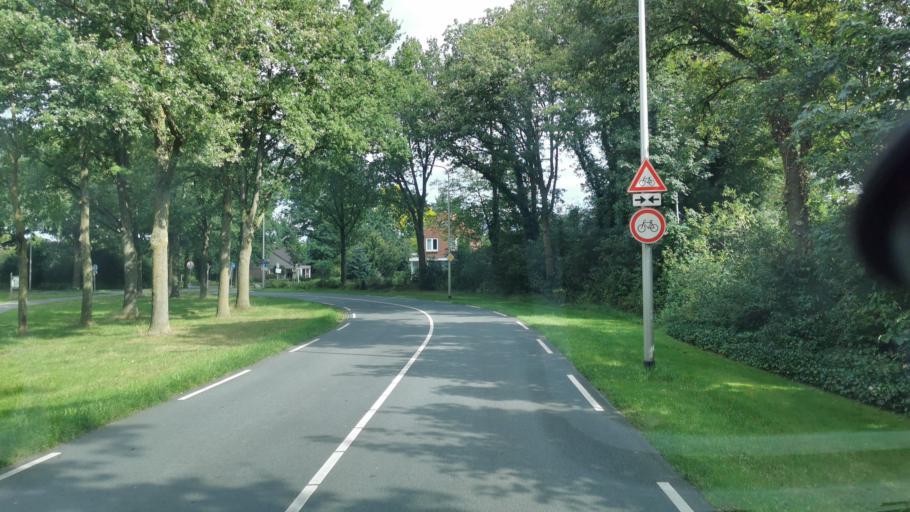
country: NL
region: Overijssel
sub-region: Gemeente Oldenzaal
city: Oldenzaal
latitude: 52.3153
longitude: 6.8944
